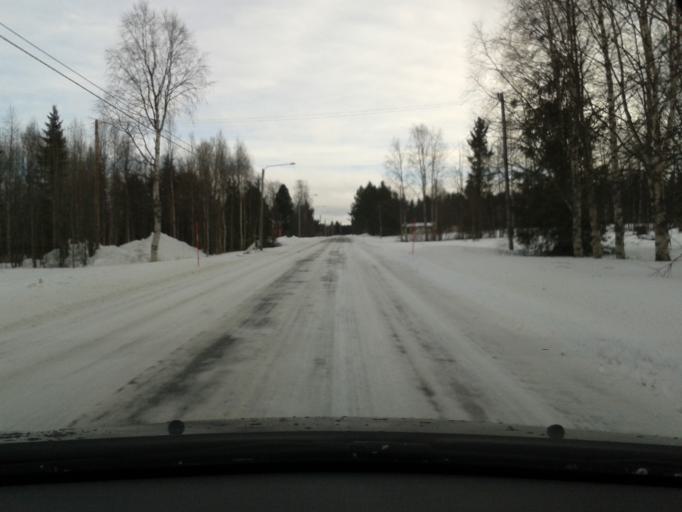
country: SE
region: Vaesterbotten
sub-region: Vilhelmina Kommun
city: Sjoberg
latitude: 64.6492
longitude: 16.3380
